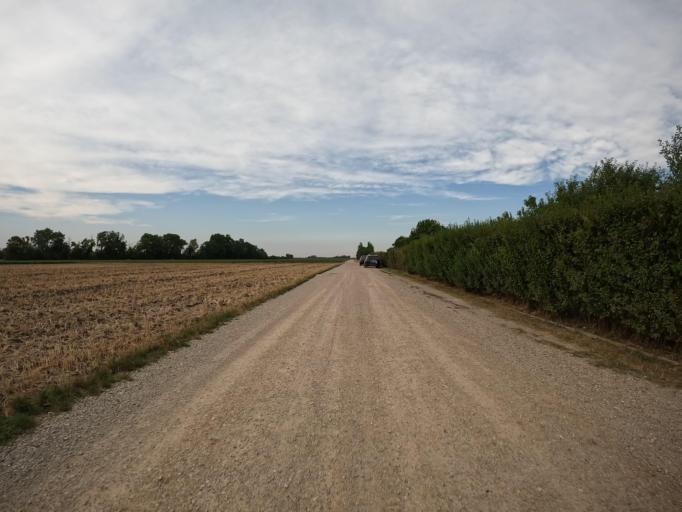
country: AT
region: Lower Austria
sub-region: Politischer Bezirk Baden
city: Trumau
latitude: 47.9986
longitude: 16.3354
